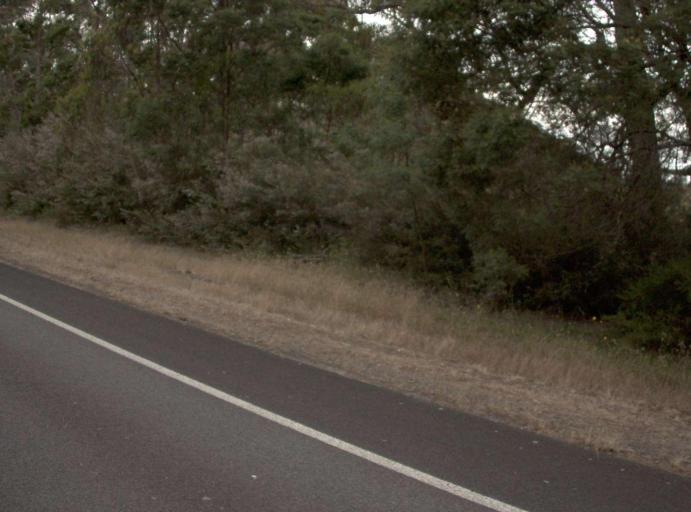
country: AU
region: Victoria
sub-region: Wellington
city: Sale
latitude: -38.5066
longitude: 146.8923
